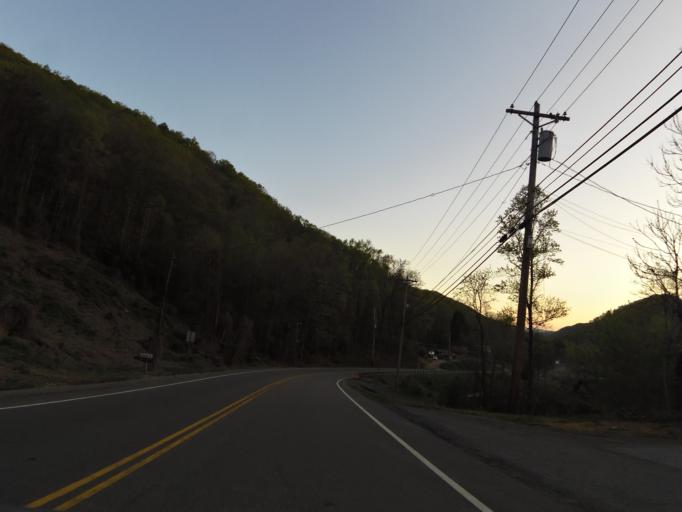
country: US
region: Tennessee
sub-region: Campbell County
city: LaFollette
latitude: 36.3990
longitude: -84.1232
